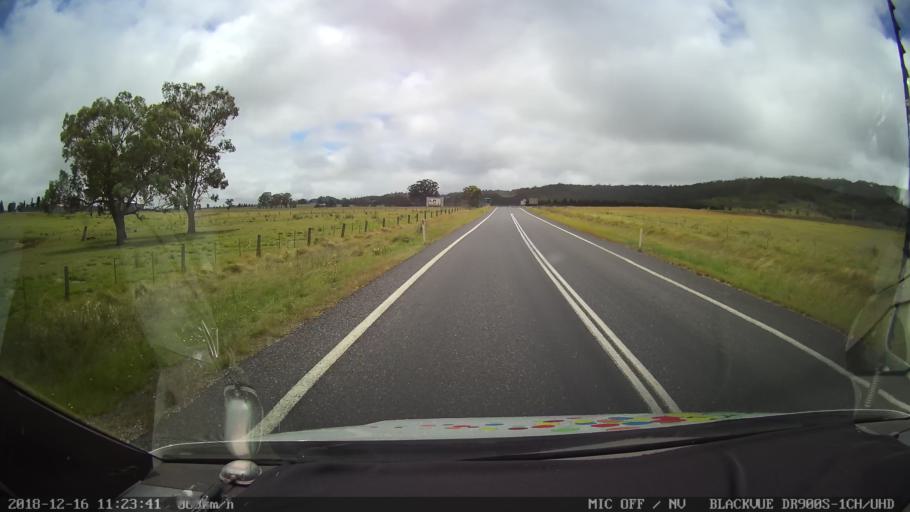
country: AU
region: New South Wales
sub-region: Tenterfield Municipality
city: Carrolls Creek
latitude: -29.0548
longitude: 152.0389
